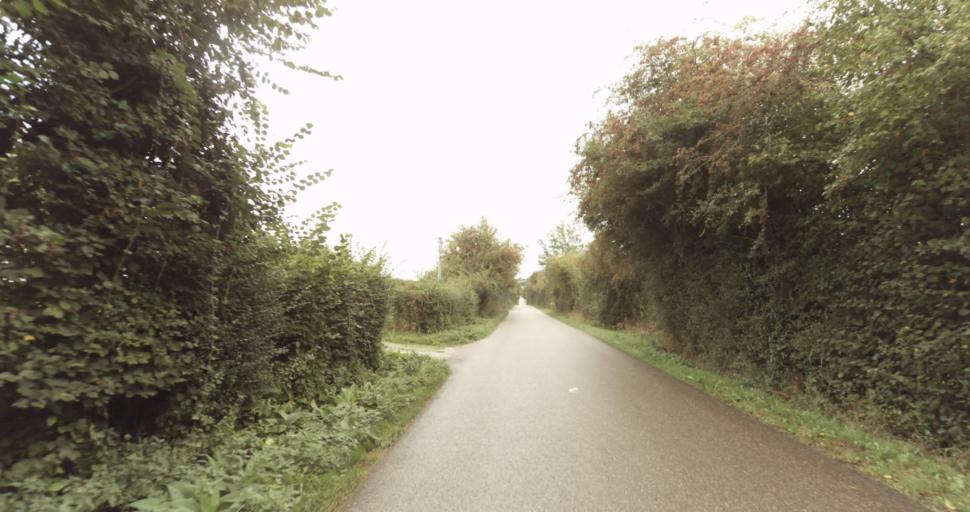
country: FR
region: Lower Normandy
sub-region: Departement de l'Orne
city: Vimoutiers
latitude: 48.8650
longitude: 0.2238
